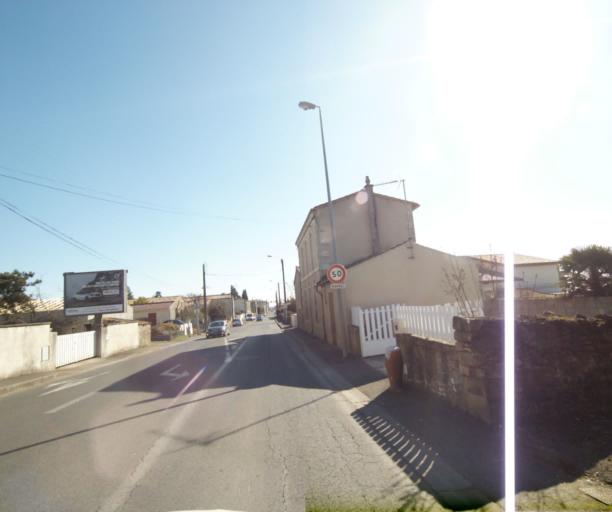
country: FR
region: Poitou-Charentes
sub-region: Departement des Deux-Sevres
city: Niort
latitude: 46.3502
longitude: -0.4781
